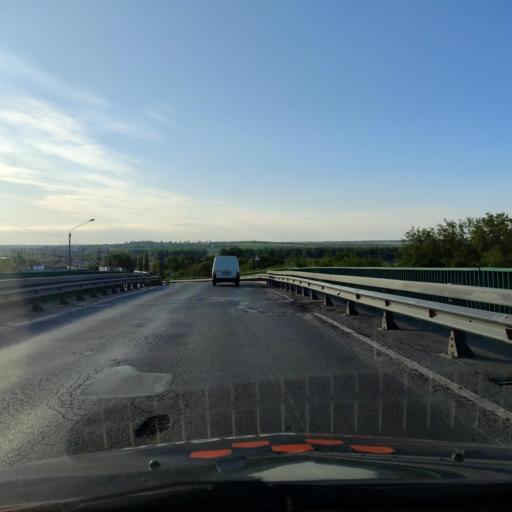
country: RU
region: Lipetsk
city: Yelets
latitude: 52.5915
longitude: 38.4929
